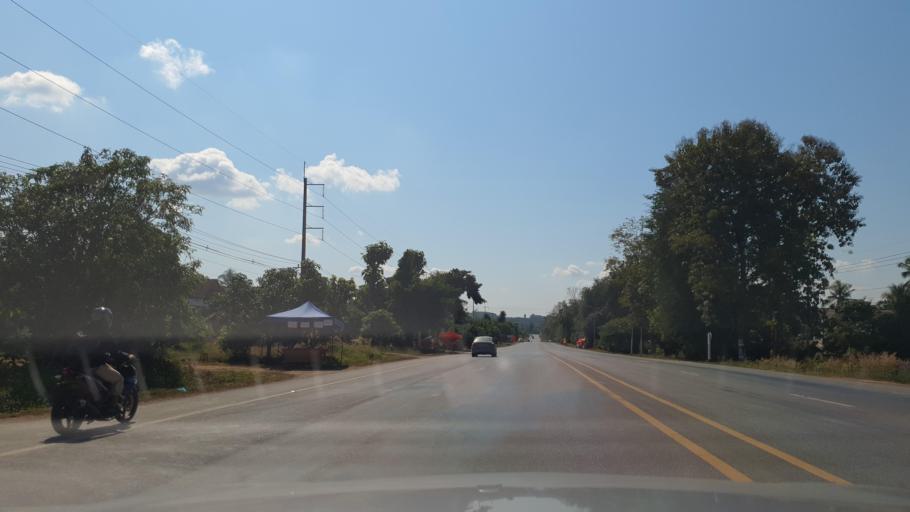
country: TH
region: Nan
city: Tha Wang Pha
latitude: 19.0337
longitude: 100.8010
